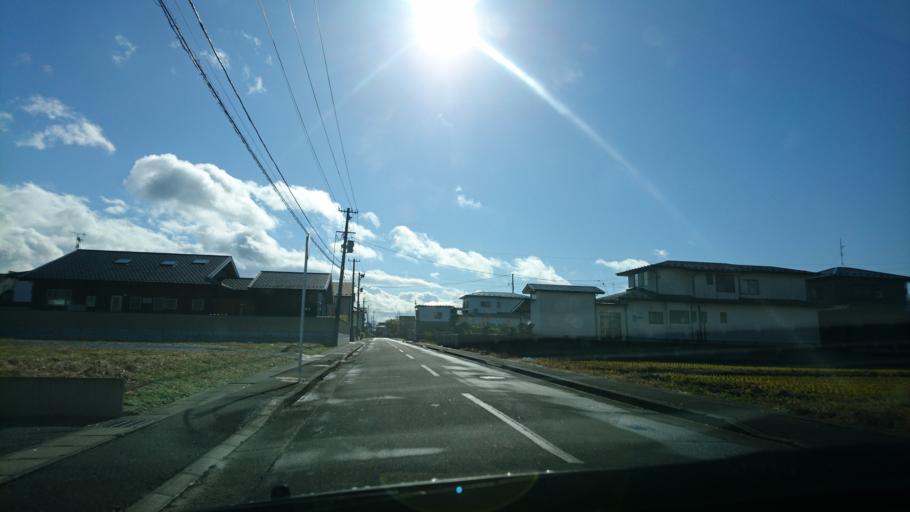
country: JP
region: Iwate
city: Ichinoseki
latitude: 38.9426
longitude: 141.1315
